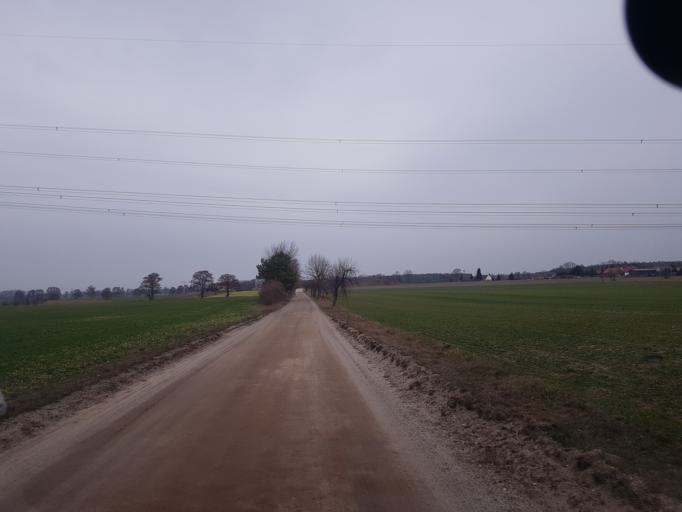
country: DE
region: Brandenburg
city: Finsterwalde
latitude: 51.6582
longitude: 13.6765
